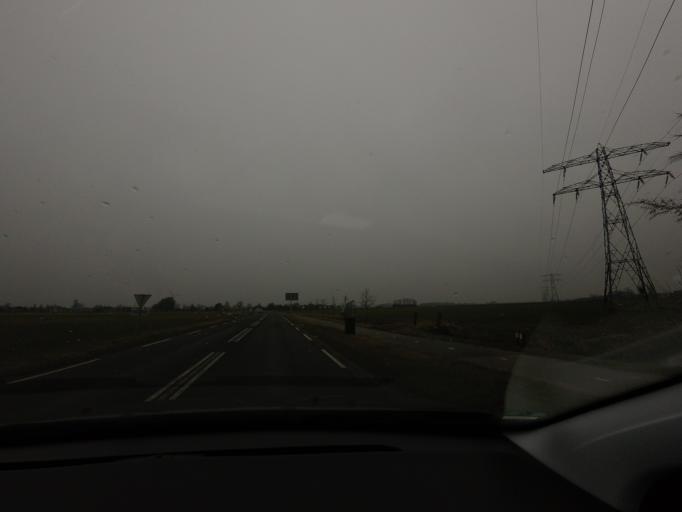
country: NL
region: Friesland
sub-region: Gemeente Franekeradeel
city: Franeker
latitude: 53.1750
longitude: 5.5527
